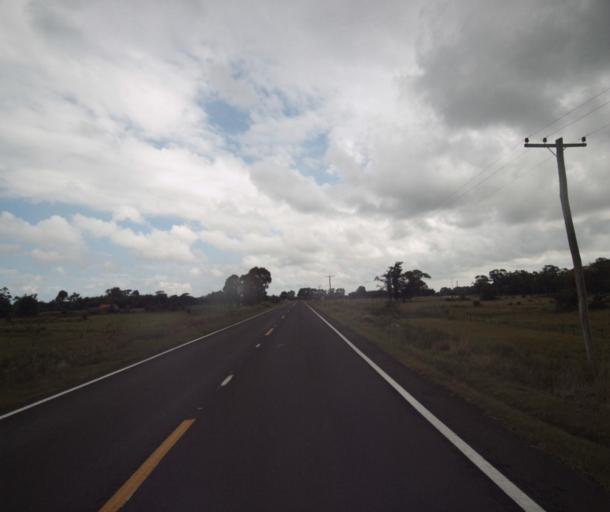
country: BR
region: Rio Grande do Sul
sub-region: Tapes
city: Tapes
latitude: -31.3187
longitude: -51.1217
